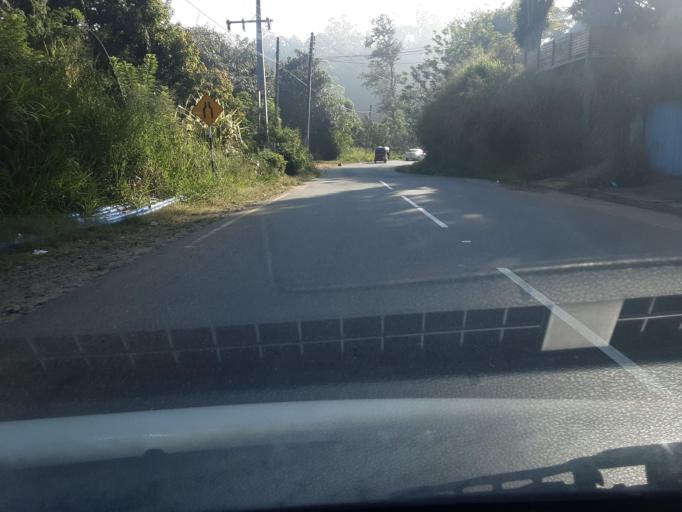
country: LK
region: Uva
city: Haputale
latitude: 6.9095
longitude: 80.9219
